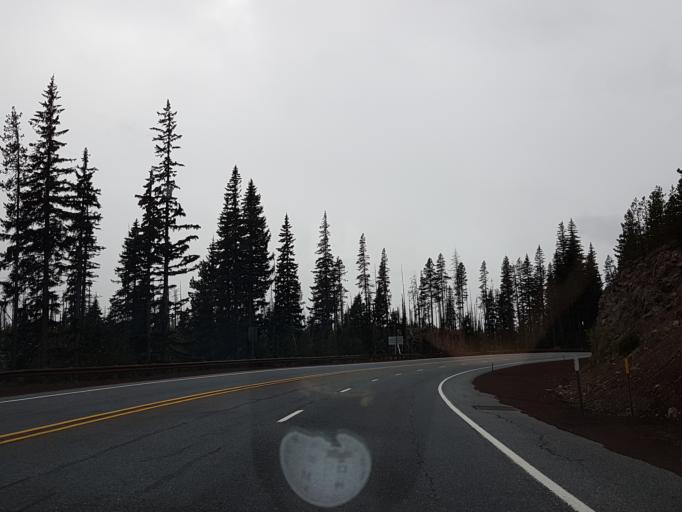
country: US
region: Oregon
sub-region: Deschutes County
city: Sisters
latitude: 44.4238
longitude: -121.8258
